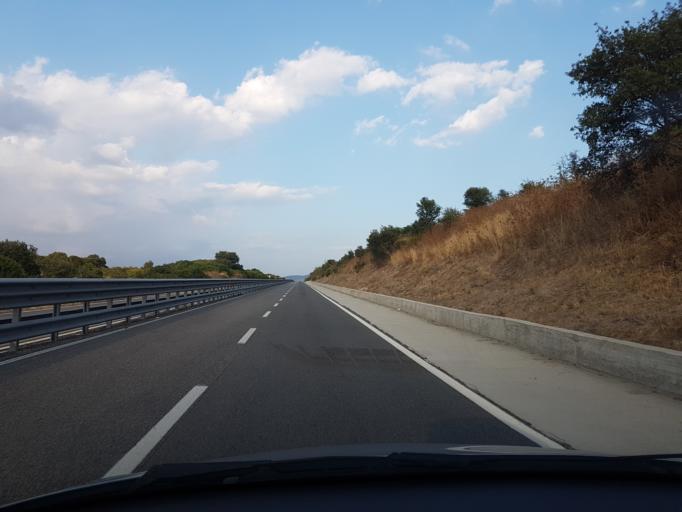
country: IT
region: Sardinia
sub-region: Provincia di Nuoro
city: Ottana
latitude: 40.2452
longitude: 9.0581
